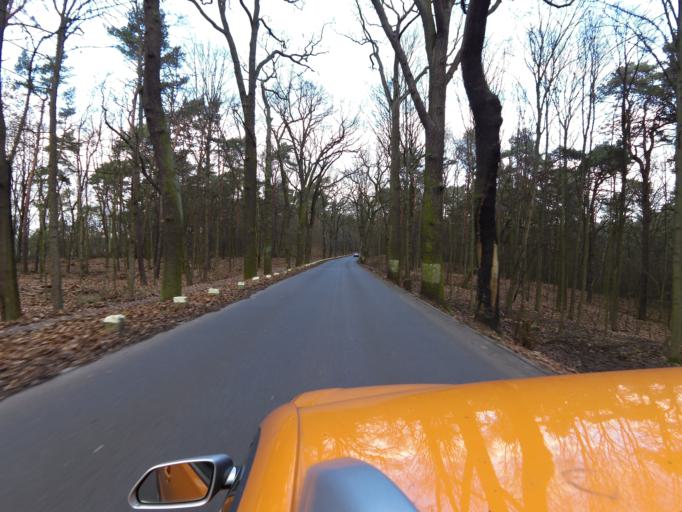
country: DE
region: Berlin
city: Gatow
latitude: 52.4825
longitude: 13.1970
